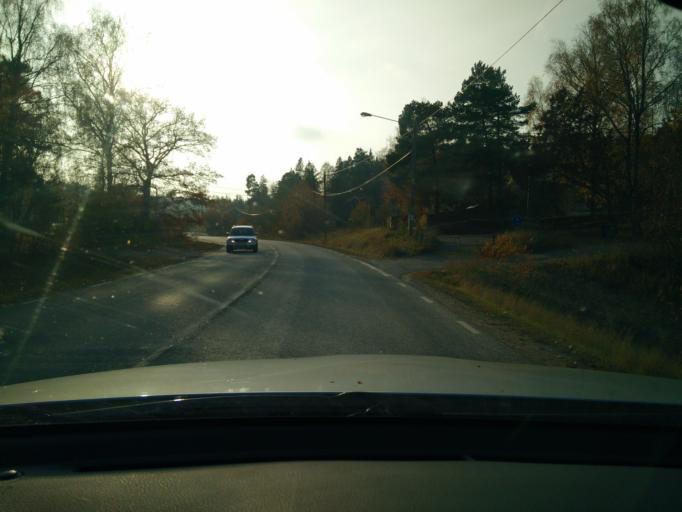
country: SE
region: Stockholm
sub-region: Sollentuna Kommun
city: Sollentuna
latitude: 59.4606
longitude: 17.9734
